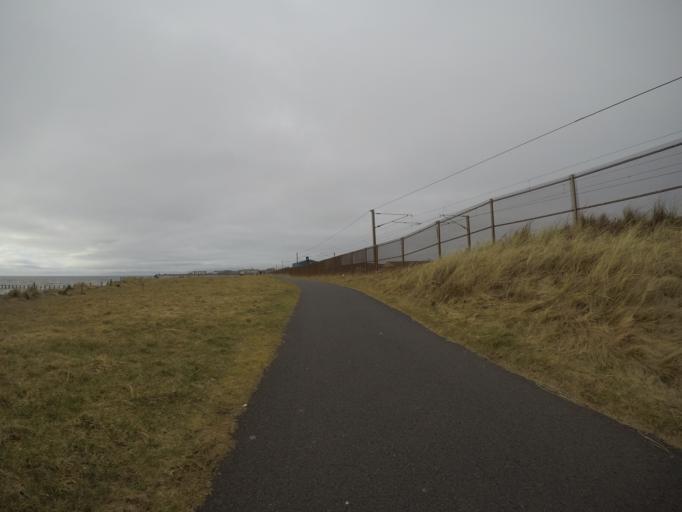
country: GB
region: Scotland
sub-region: North Ayrshire
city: Stevenston
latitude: 55.6325
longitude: -4.7671
